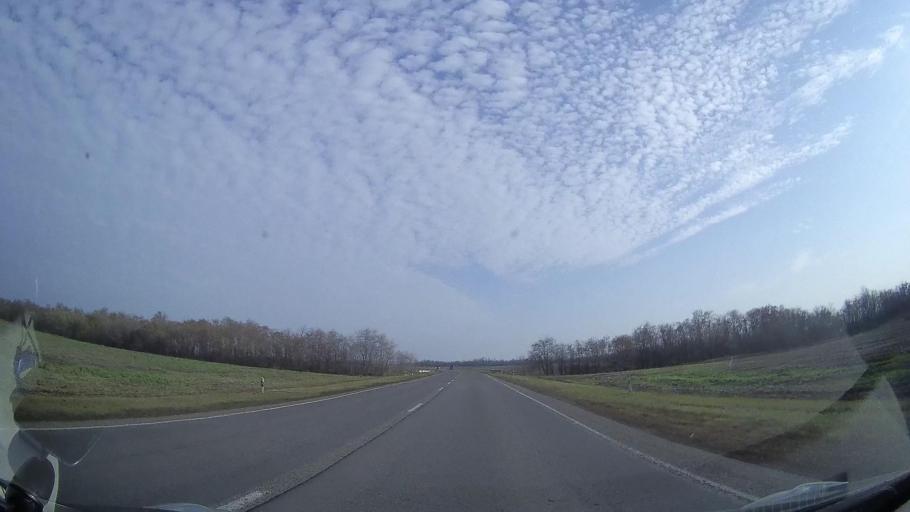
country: RU
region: Rostov
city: Tselina
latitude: 46.5108
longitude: 41.0130
